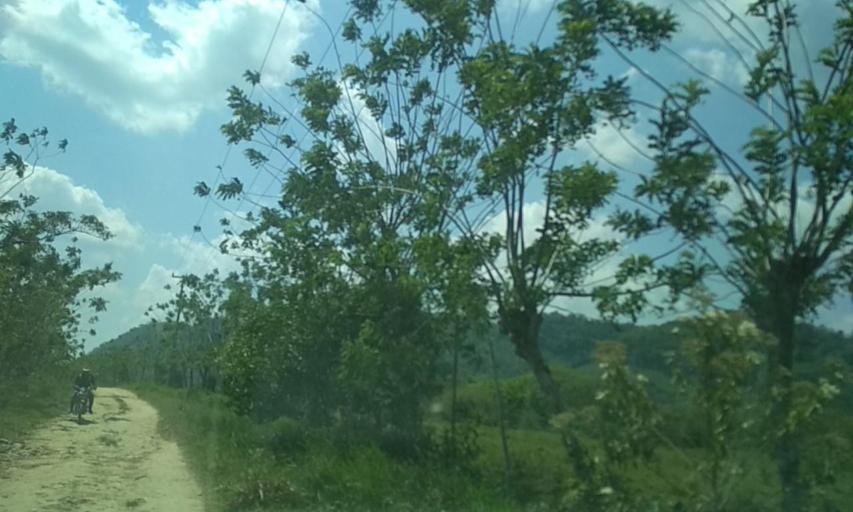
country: MX
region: Chiapas
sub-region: Tecpatan
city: Raudales Malpaso
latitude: 17.2991
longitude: -93.8107
